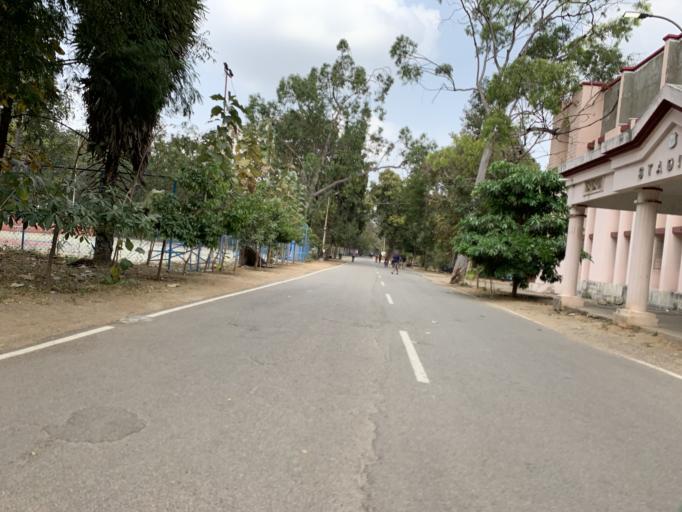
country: IN
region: Telangana
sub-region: Warangal
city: Warangal
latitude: 17.9805
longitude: 79.5322
